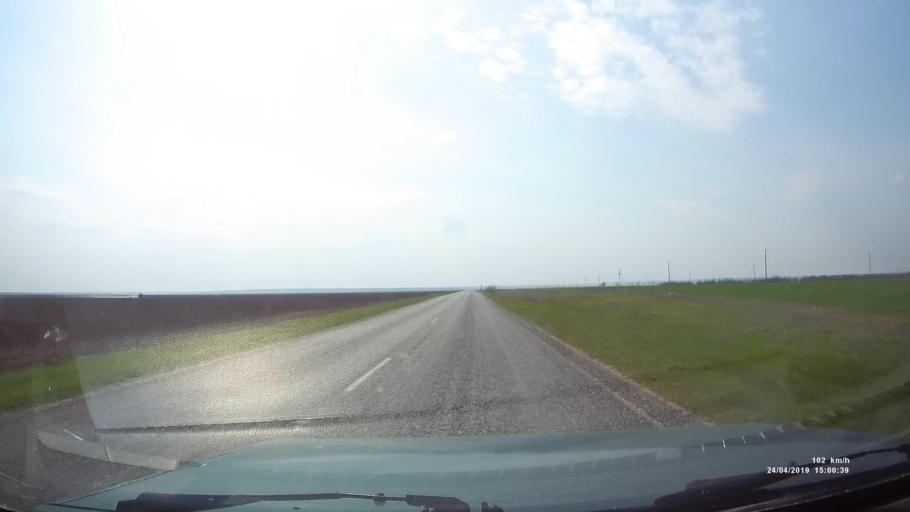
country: RU
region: Rostov
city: Remontnoye
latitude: 46.5655
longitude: 43.5512
